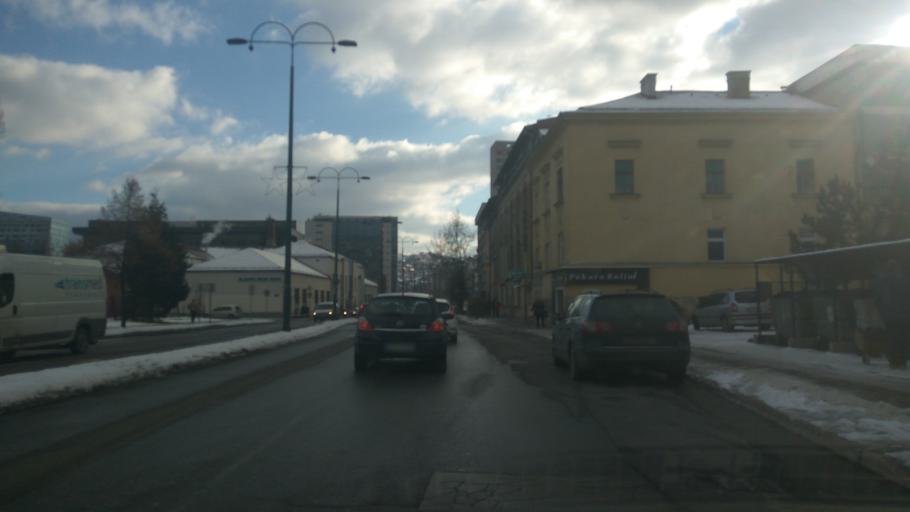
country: BA
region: Federation of Bosnia and Herzegovina
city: Kobilja Glava
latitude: 43.8560
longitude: 18.3844
